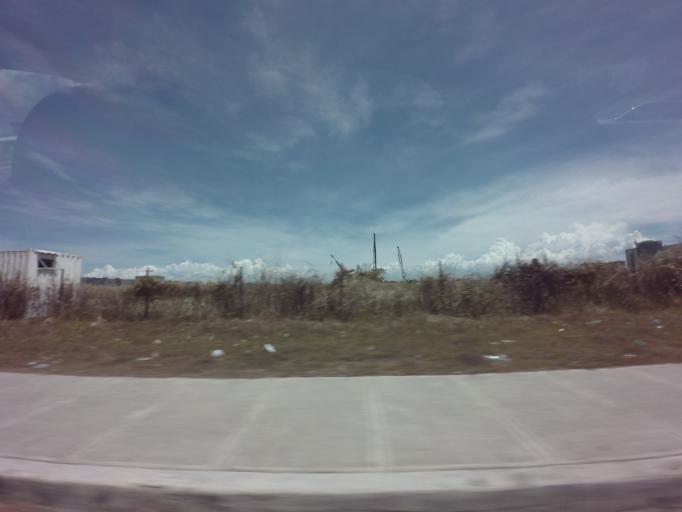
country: PH
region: Metro Manila
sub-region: Makati City
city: Makati City
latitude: 14.5174
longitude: 120.9864
